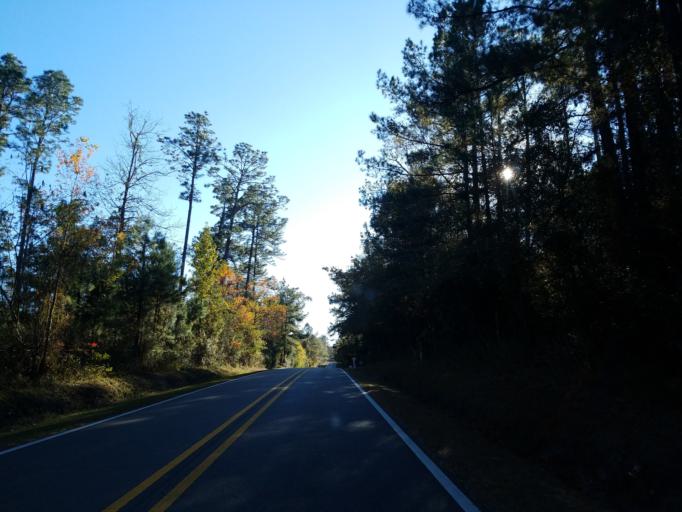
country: US
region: Mississippi
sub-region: Forrest County
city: Hattiesburg
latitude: 31.2501
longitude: -89.2956
